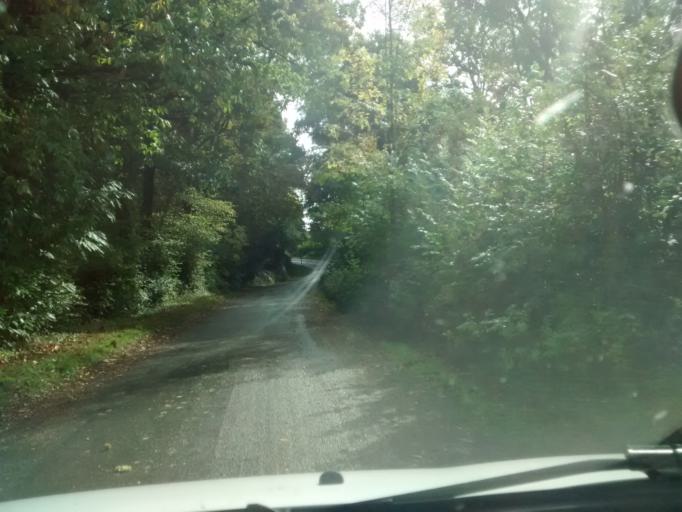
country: FR
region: Brittany
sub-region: Departement d'Ille-et-Vilaine
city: Chateaubourg
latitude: 48.1224
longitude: -1.3912
